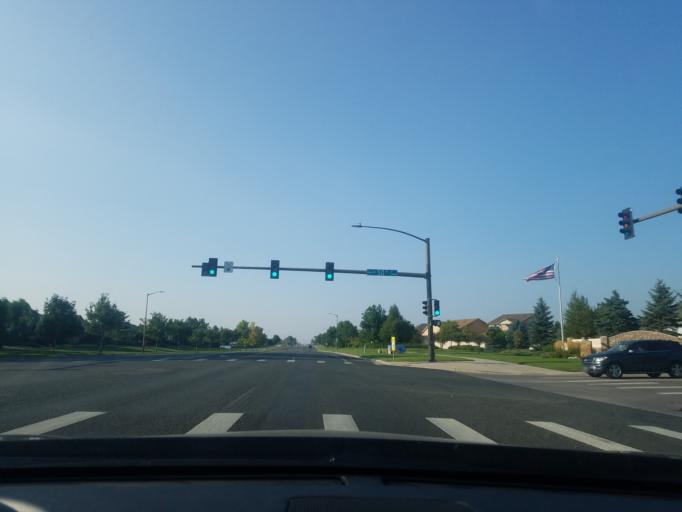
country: US
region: Colorado
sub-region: Larimer County
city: Loveland
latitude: 40.4435
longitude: -105.0963
